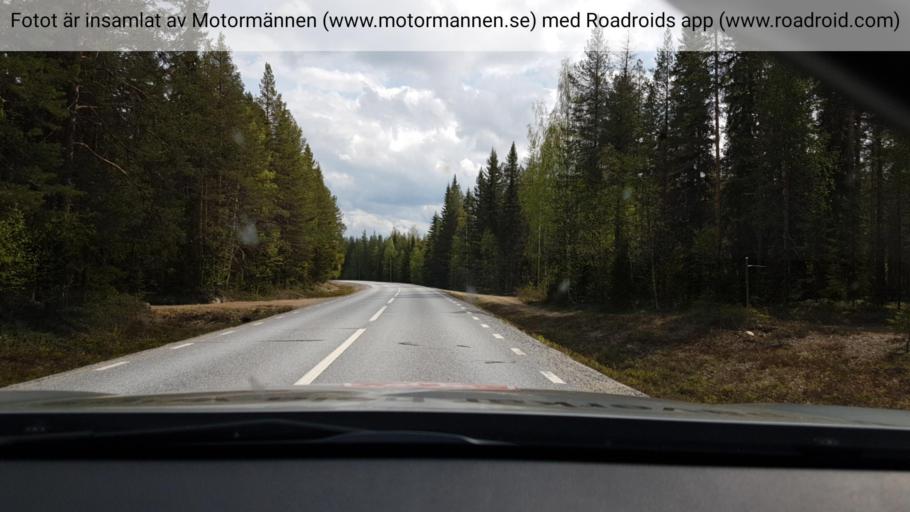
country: SE
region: Vaesterbotten
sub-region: Lycksele Kommun
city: Lycksele
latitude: 64.0624
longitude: 18.4467
